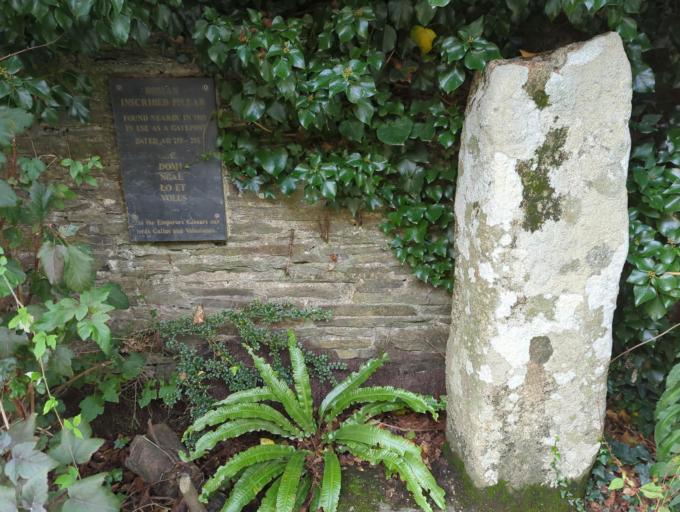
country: GB
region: England
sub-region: Cornwall
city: Tintagel
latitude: 50.6701
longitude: -4.7240
